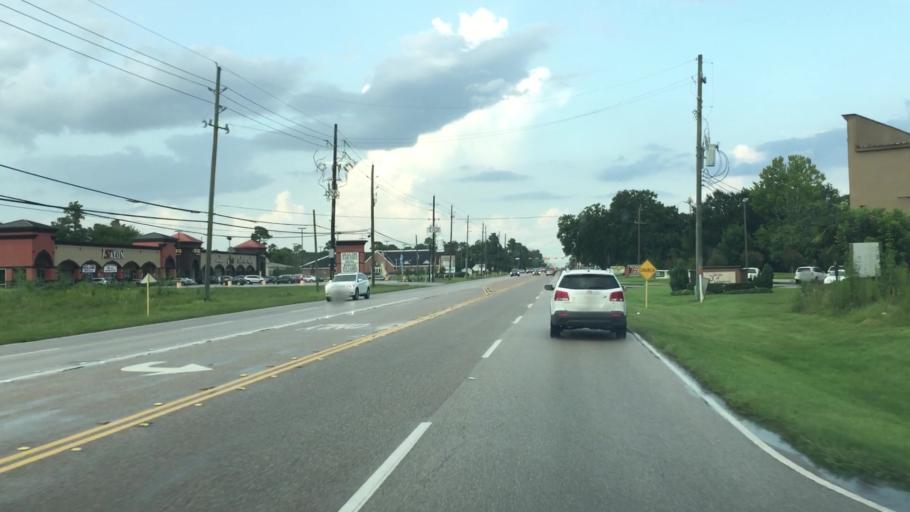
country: US
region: Texas
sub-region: Harris County
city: Spring
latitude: 30.0305
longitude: -95.5064
